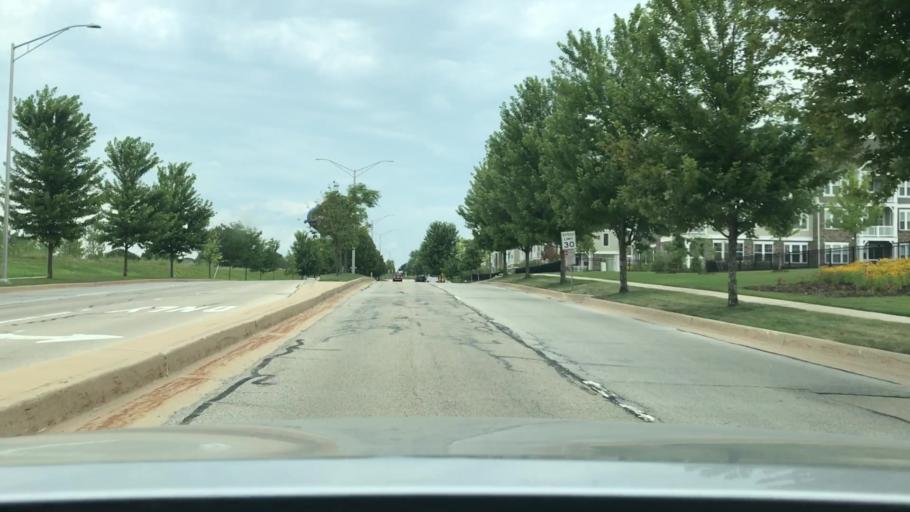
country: US
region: Illinois
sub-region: Will County
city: Bolingbrook
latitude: 41.7132
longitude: -88.0395
